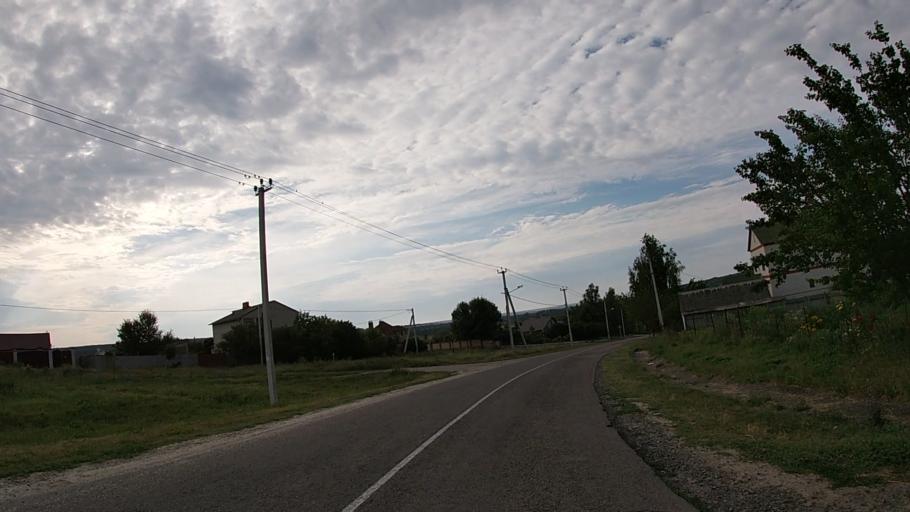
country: RU
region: Belgorod
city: Severnyy
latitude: 50.7142
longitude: 36.5947
